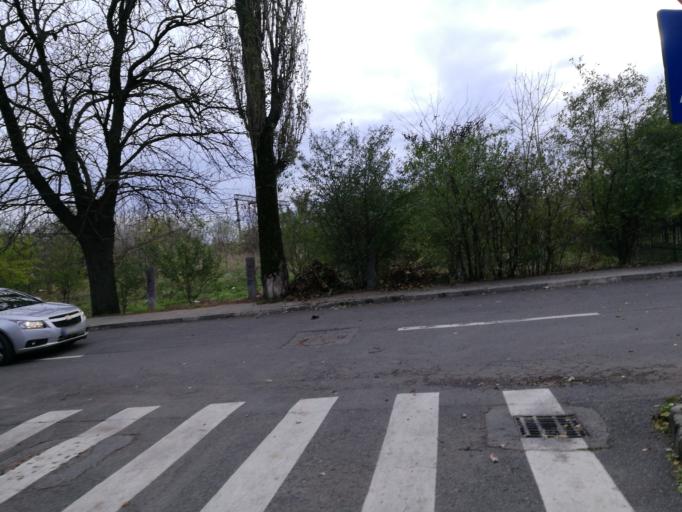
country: RO
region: Ilfov
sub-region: Comuna Chiajna
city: Rosu
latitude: 44.4767
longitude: 26.0295
